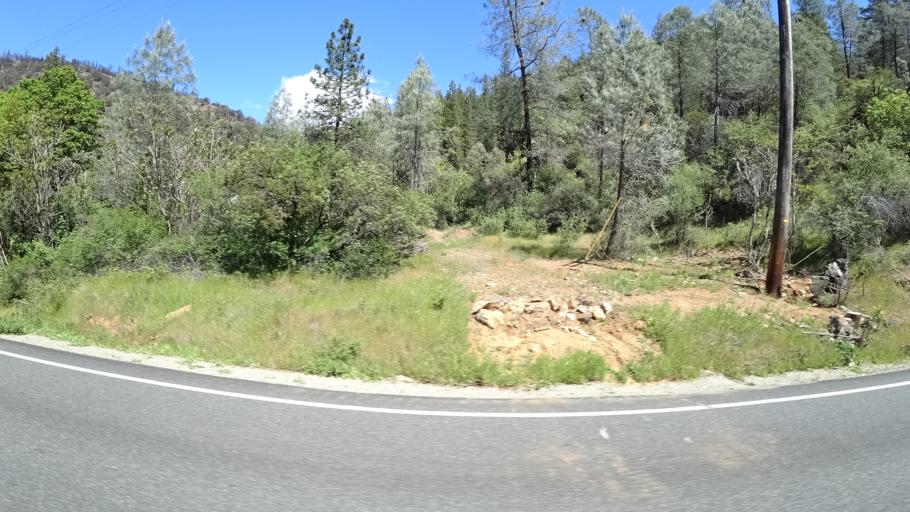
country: US
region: California
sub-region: Trinity County
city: Weaverville
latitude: 40.7529
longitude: -123.0657
